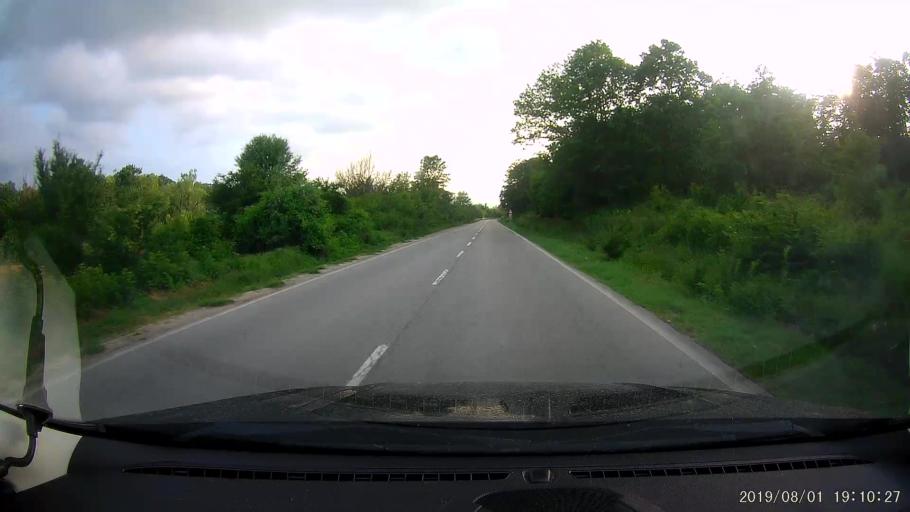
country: BG
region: Shumen
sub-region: Obshtina Smyadovo
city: Smyadovo
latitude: 42.9801
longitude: 26.9791
